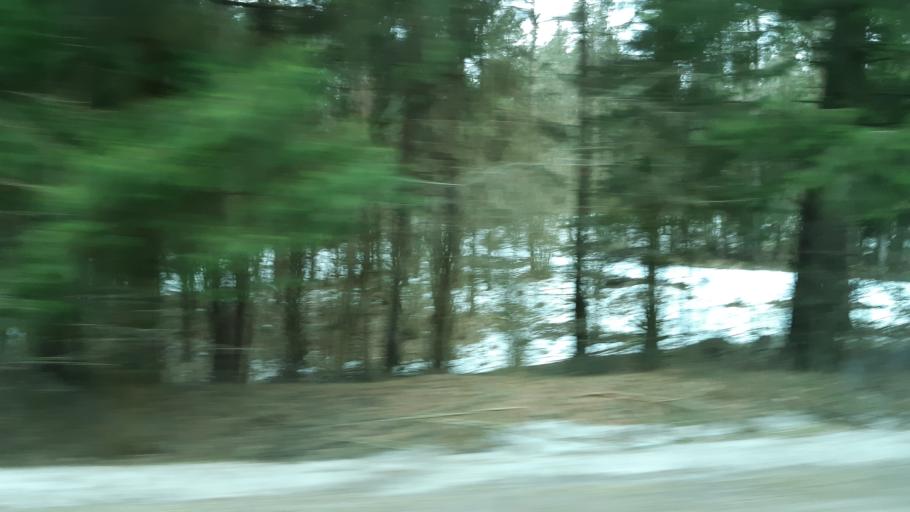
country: PL
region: Podlasie
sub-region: Suwalki
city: Suwalki
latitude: 54.2883
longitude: 22.9542
